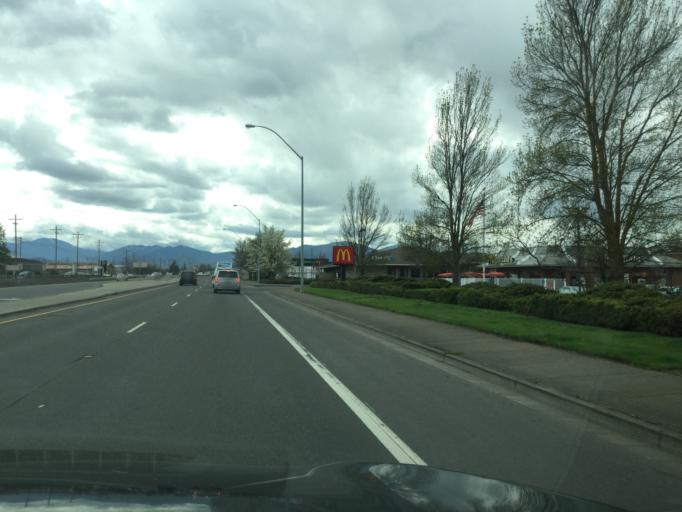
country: US
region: Oregon
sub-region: Jackson County
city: Medford
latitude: 42.3671
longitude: -122.8561
